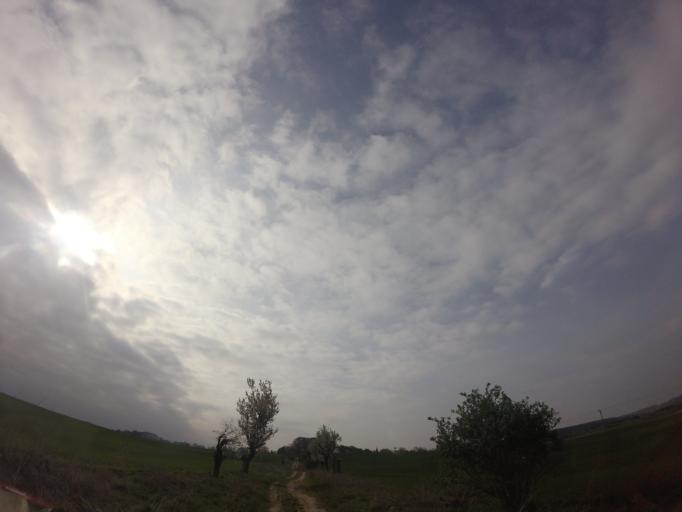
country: PL
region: West Pomeranian Voivodeship
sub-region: Powiat choszczenski
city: Pelczyce
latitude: 53.0718
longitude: 15.2403
